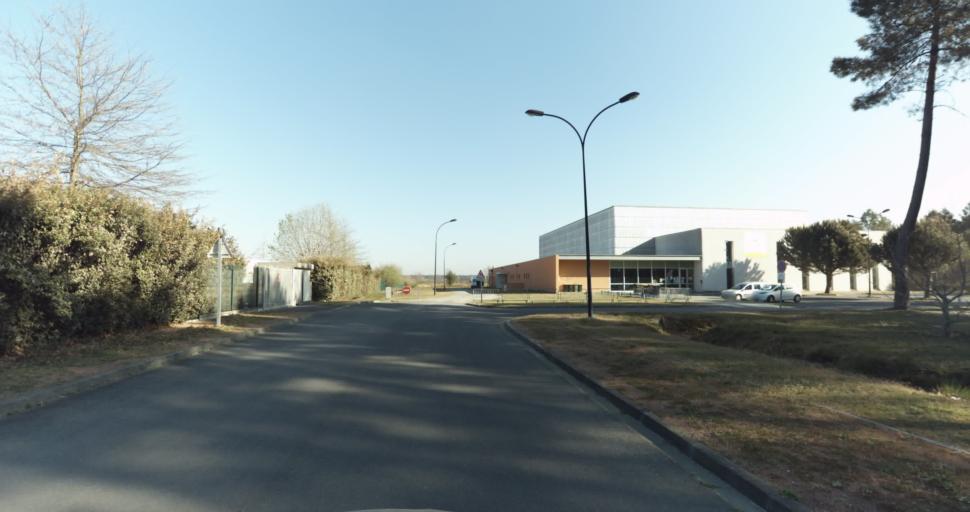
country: FR
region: Aquitaine
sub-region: Departement de la Gironde
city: Martignas-sur-Jalle
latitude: 44.8066
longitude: -0.8065
